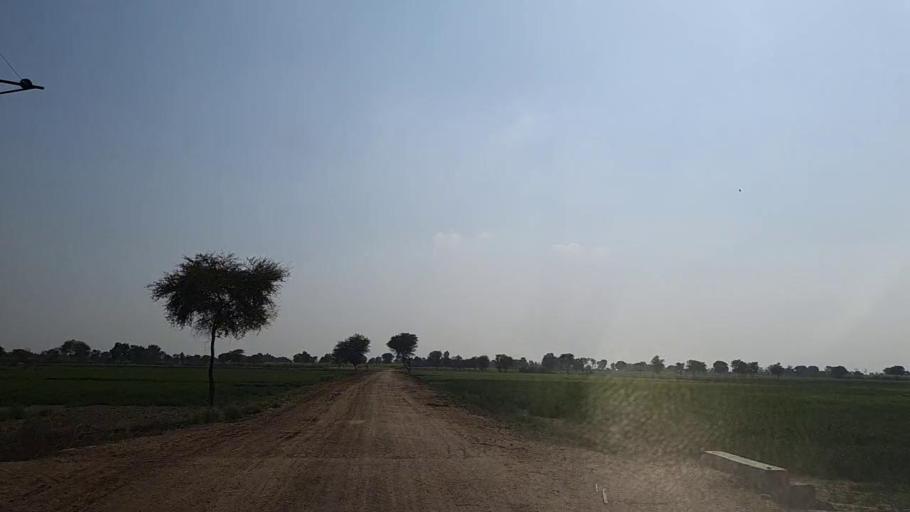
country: PK
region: Sindh
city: Daur
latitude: 26.4328
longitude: 68.2344
